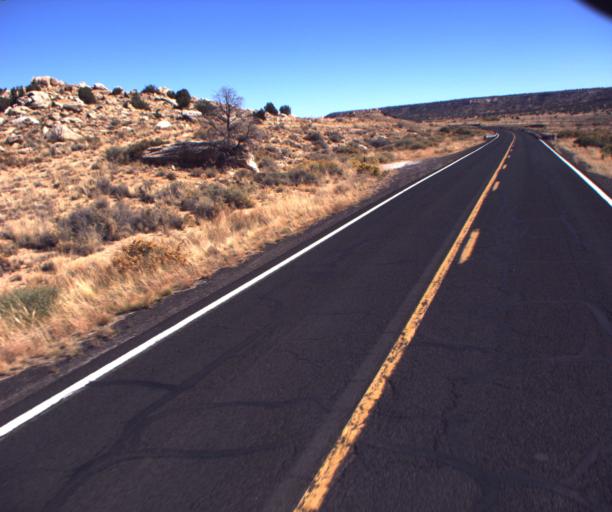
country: US
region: Arizona
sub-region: Navajo County
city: First Mesa
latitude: 35.8300
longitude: -110.2854
